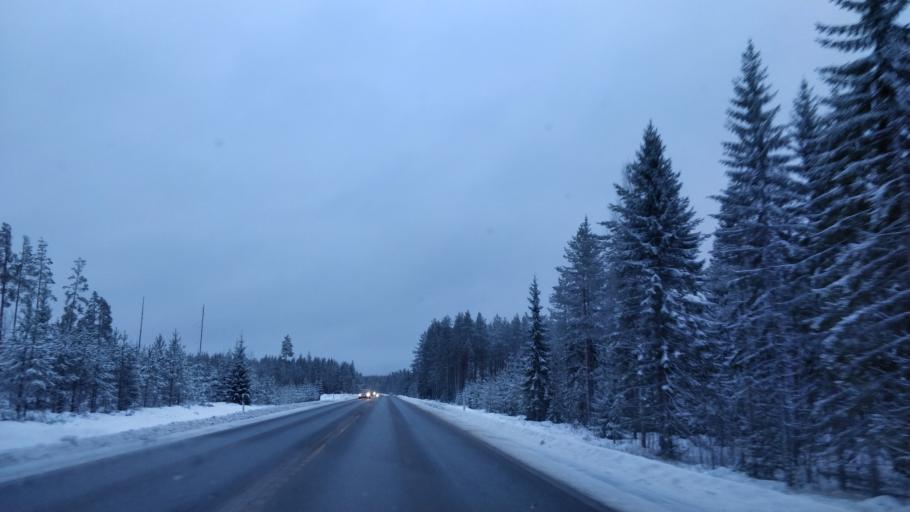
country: FI
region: Central Finland
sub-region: Saarijaervi-Viitasaari
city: Pihtipudas
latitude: 63.2168
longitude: 25.6735
